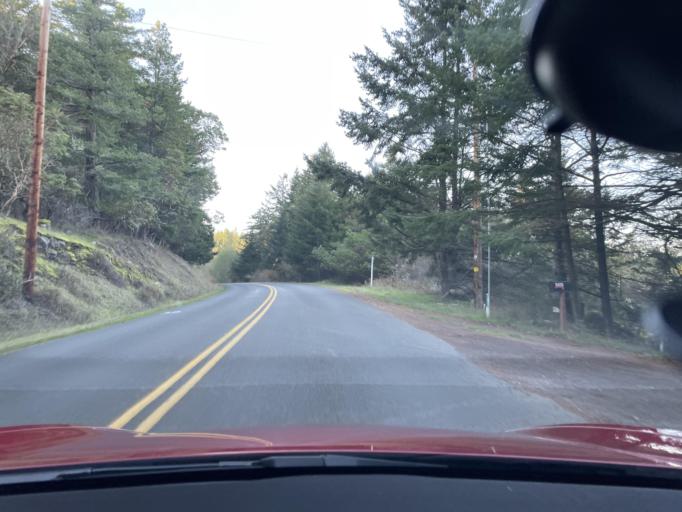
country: US
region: Washington
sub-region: San Juan County
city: Friday Harbor
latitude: 48.5578
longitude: -123.1644
